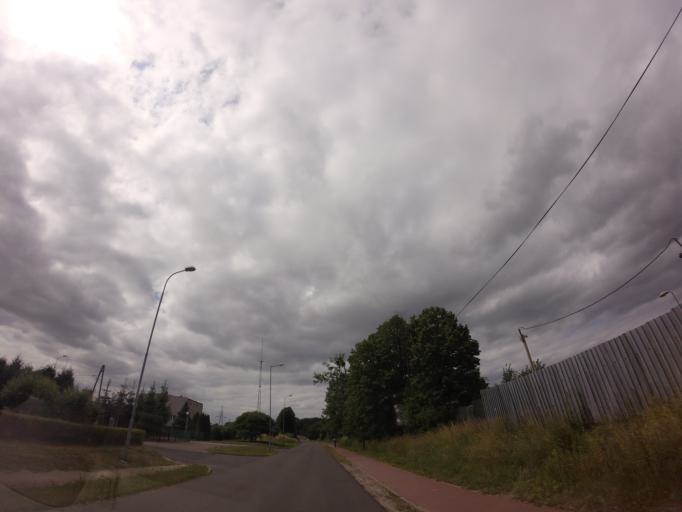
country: PL
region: Lubusz
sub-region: Powiat strzelecko-drezdenecki
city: Strzelce Krajenskie
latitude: 52.8692
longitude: 15.5282
